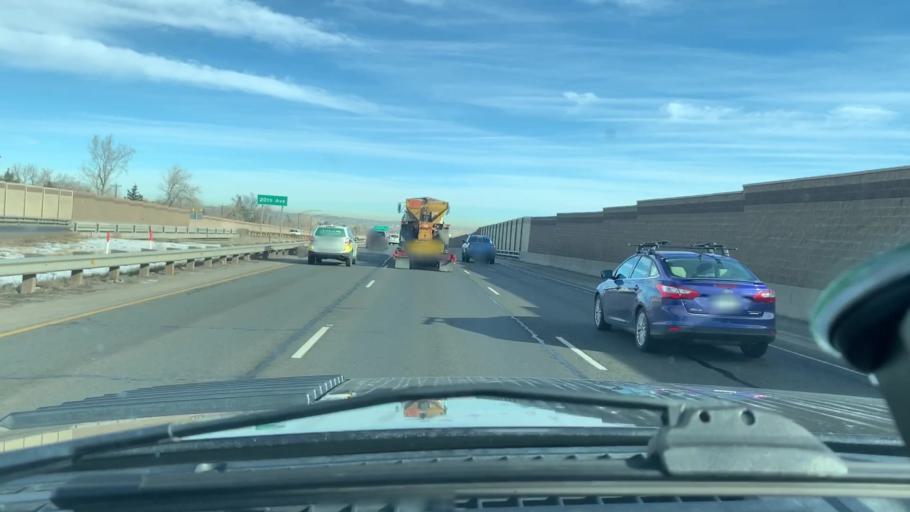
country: US
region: Colorado
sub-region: Jefferson County
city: Applewood
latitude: 39.7467
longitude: -105.1512
